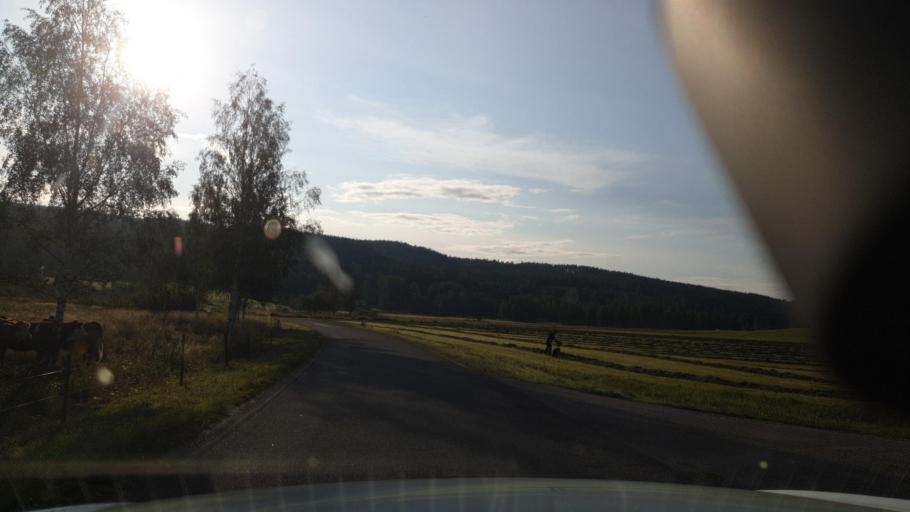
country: SE
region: Vaermland
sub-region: Arvika Kommun
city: Arvika
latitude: 59.7464
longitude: 12.6320
